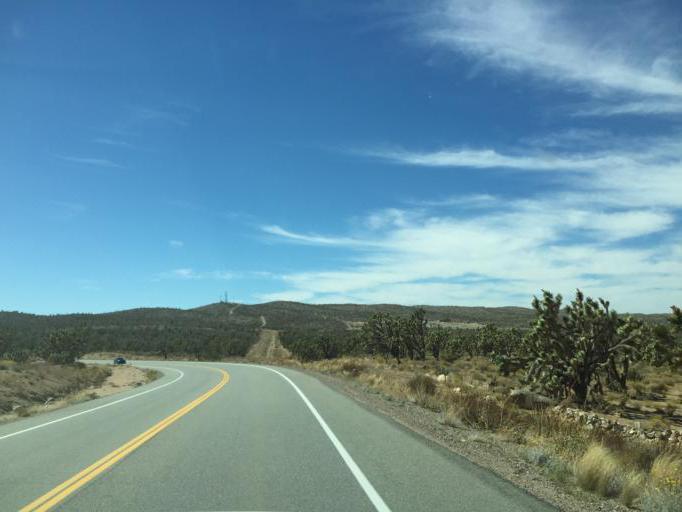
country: US
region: Arizona
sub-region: Mohave County
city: Meadview
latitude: 35.8646
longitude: -114.0774
